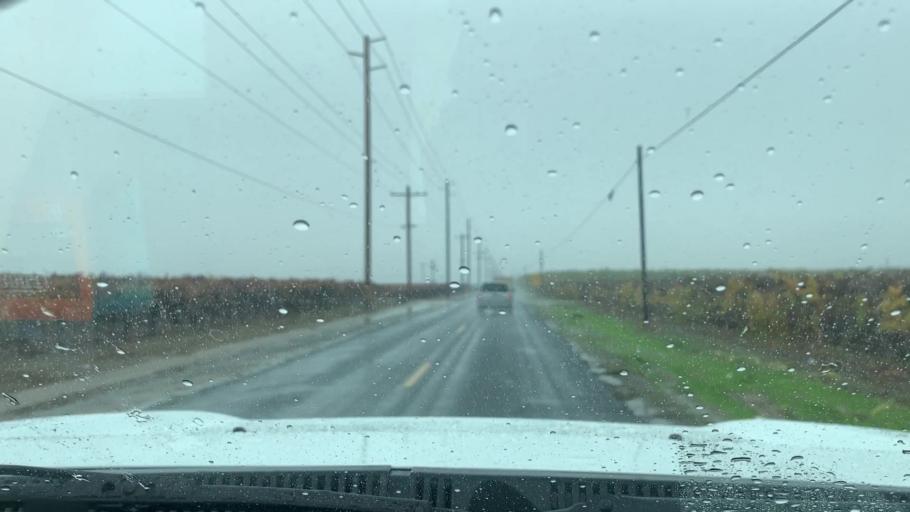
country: US
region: California
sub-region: Tulare County
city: Earlimart
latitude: 35.8340
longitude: -119.2294
